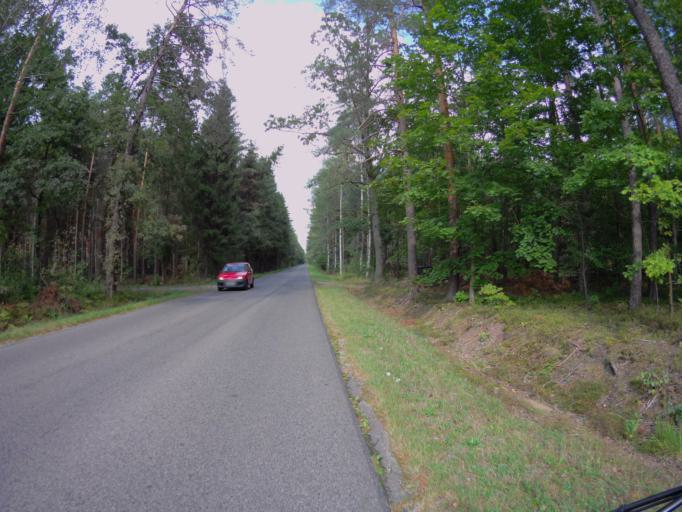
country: PL
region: Subcarpathian Voivodeship
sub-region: Powiat lezajski
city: Brzoza Krolewska
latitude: 50.2536
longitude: 22.3658
